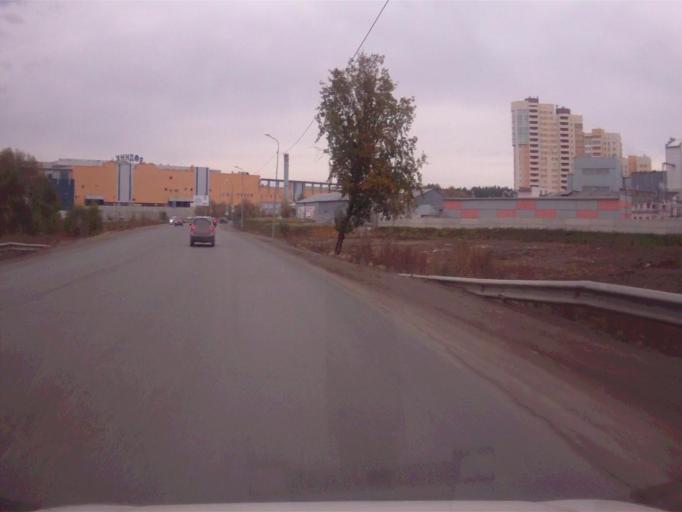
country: RU
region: Chelyabinsk
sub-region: Gorod Chelyabinsk
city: Chelyabinsk
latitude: 55.1724
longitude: 61.3496
